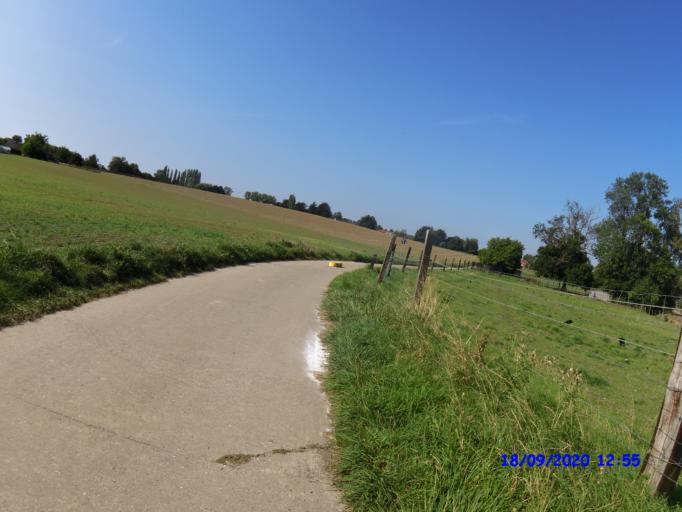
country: BE
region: Flanders
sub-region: Provincie Limburg
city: Gingelom
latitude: 50.7406
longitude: 5.1333
